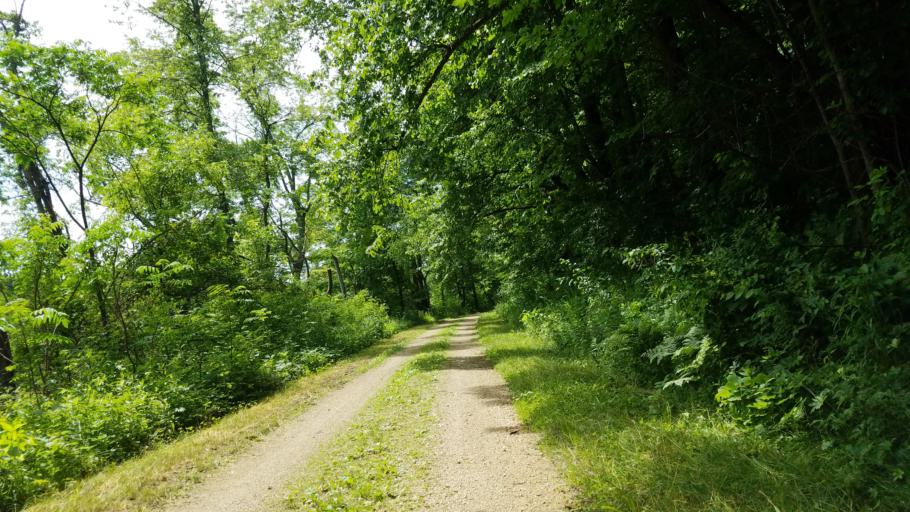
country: US
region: Wisconsin
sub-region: Dunn County
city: Menomonie
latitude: 44.8039
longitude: -91.9467
